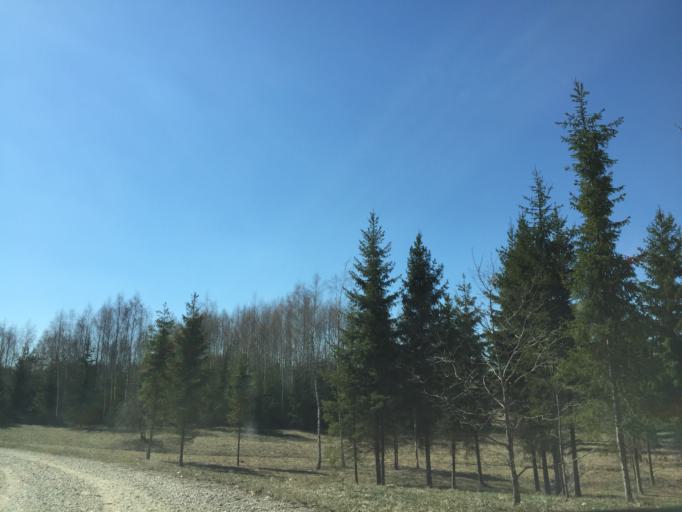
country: EE
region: Viljandimaa
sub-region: Viiratsi vald
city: Viiratsi
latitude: 58.3127
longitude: 25.6834
